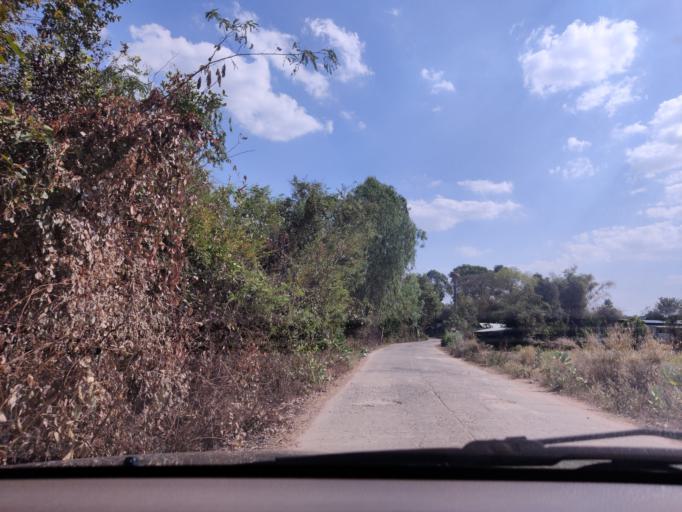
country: TH
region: Sisaket
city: Si Sa Ket
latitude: 15.0678
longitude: 104.3499
